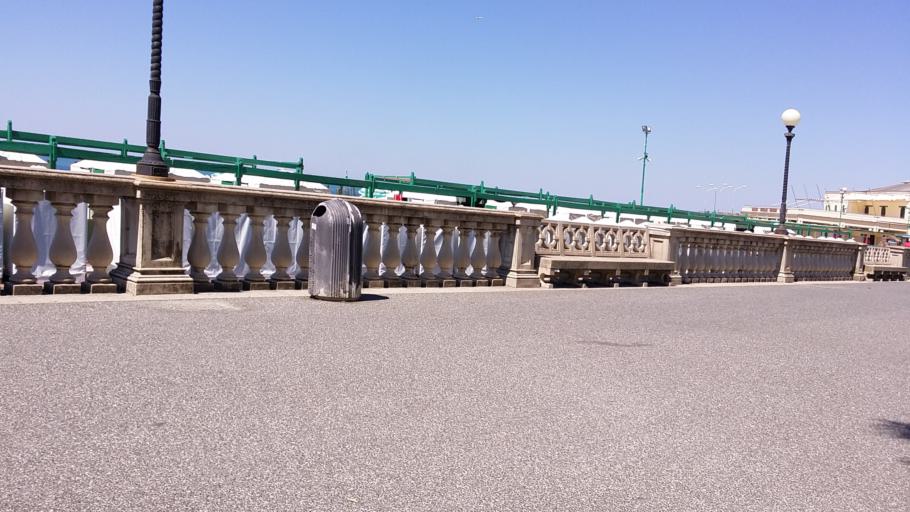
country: IT
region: Tuscany
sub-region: Provincia di Livorno
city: Livorno
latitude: 43.5312
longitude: 10.3033
